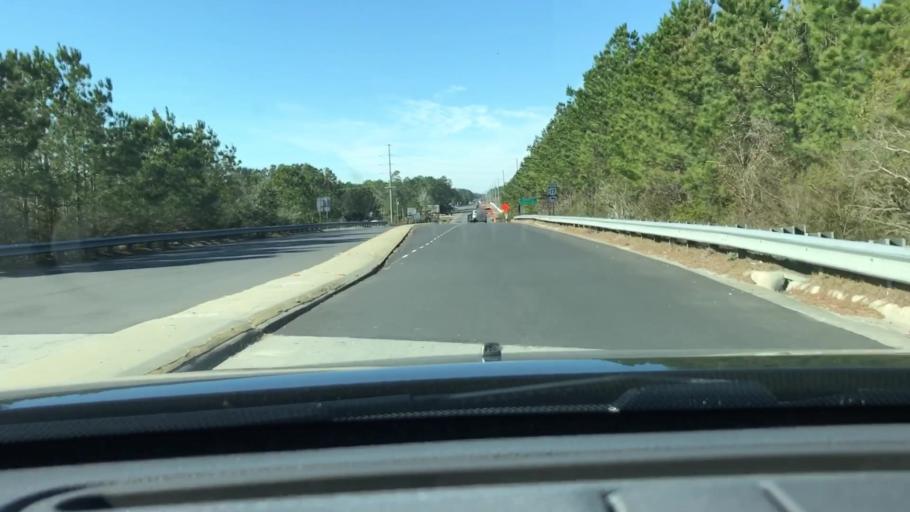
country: US
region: North Carolina
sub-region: Brunswick County
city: Shallotte
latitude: 33.9765
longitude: -78.4052
